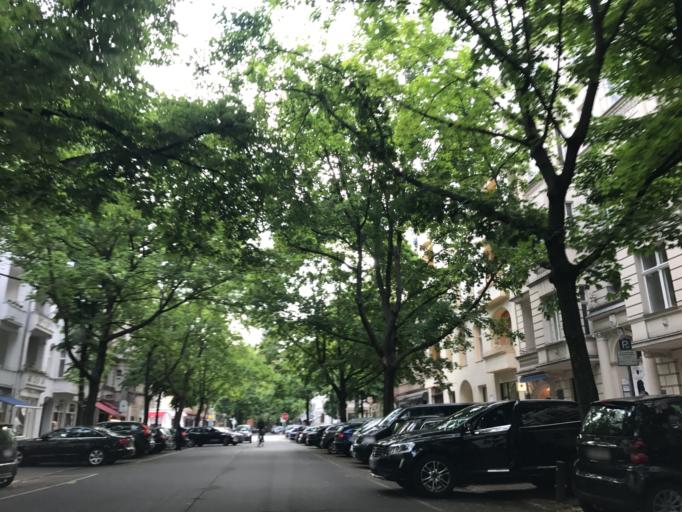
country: DE
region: Berlin
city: Wilmersdorf Bezirk
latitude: 52.4981
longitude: 13.3259
